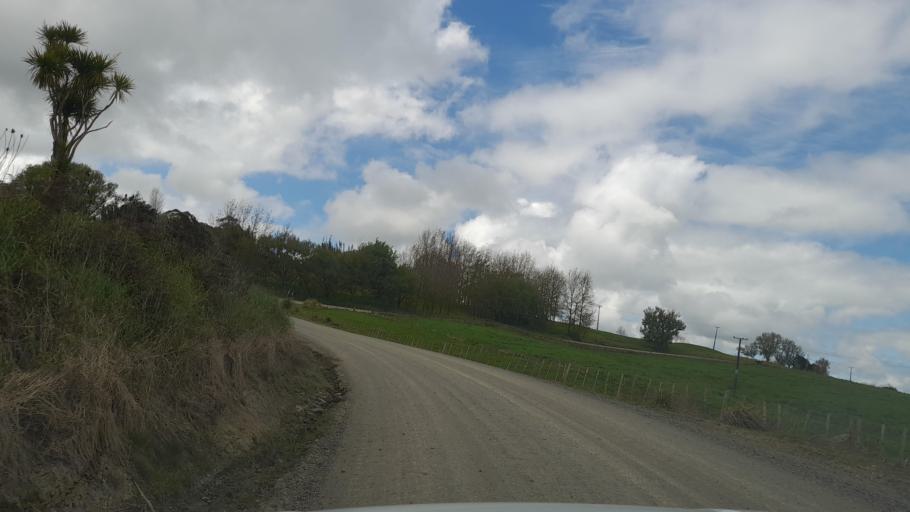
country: NZ
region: Auckland
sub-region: Auckland
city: Wellsford
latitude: -36.1650
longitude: 174.3197
